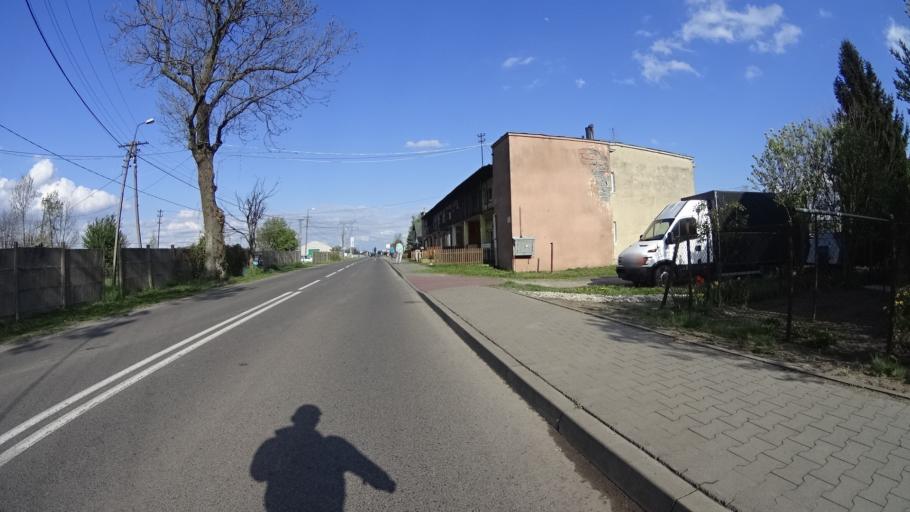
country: PL
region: Masovian Voivodeship
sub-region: Powiat warszawski zachodni
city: Jozefow
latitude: 52.2326
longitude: 20.6960
